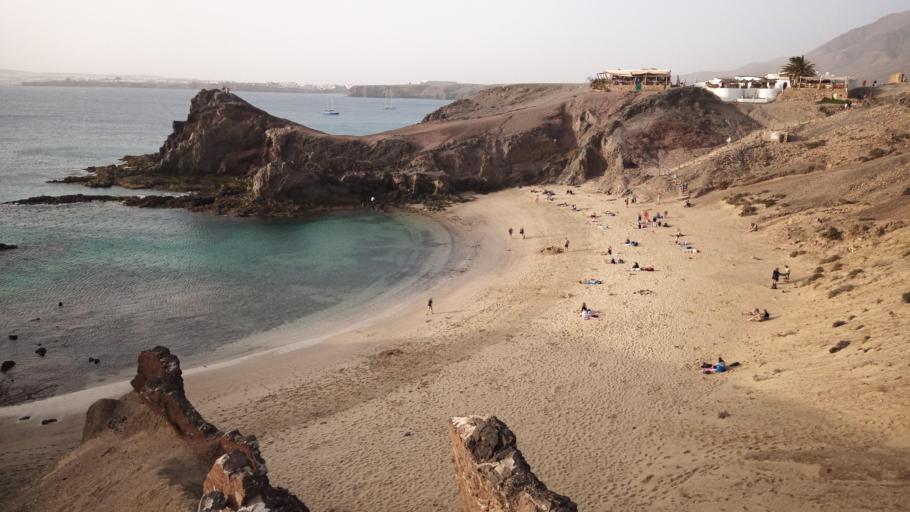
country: ES
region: Canary Islands
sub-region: Provincia de Las Palmas
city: Playa Blanca
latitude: 28.8419
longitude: -13.7879
